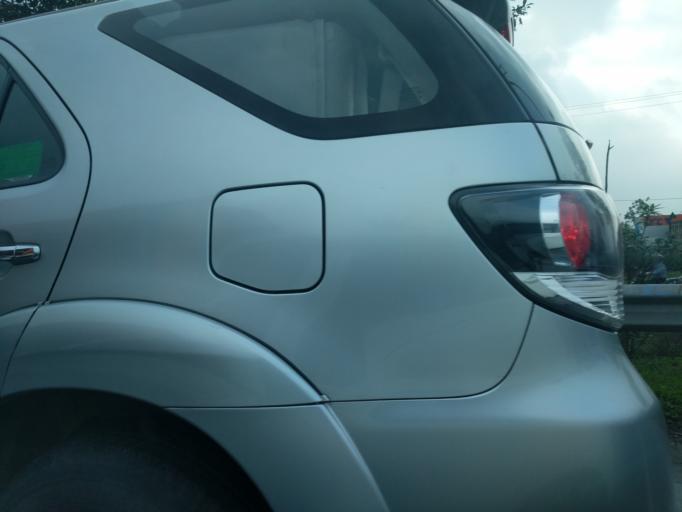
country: VN
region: Ha Noi
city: Dong Anh
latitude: 21.1841
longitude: 105.8295
